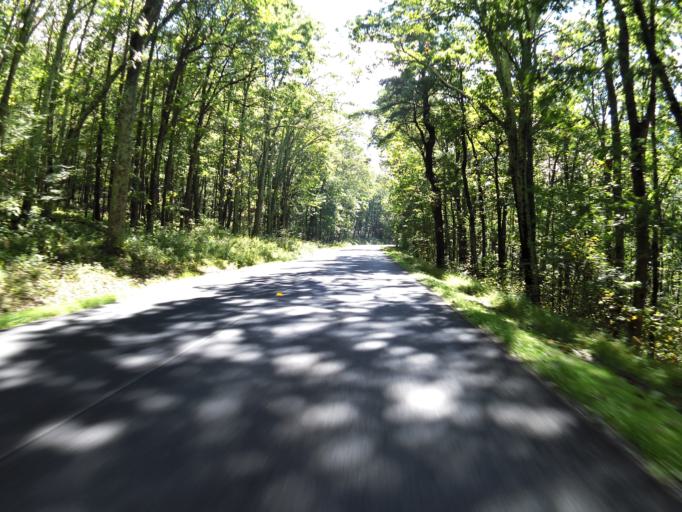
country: US
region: Virginia
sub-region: Page County
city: Luray
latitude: 38.6923
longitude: -78.3199
